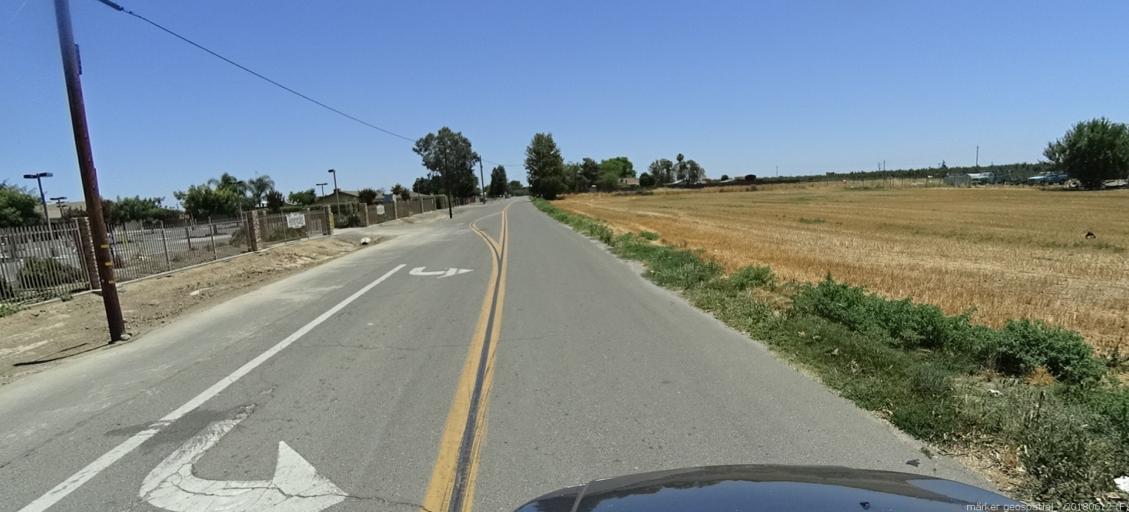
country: US
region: California
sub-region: Madera County
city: Chowchilla
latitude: 37.0929
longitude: -120.2891
